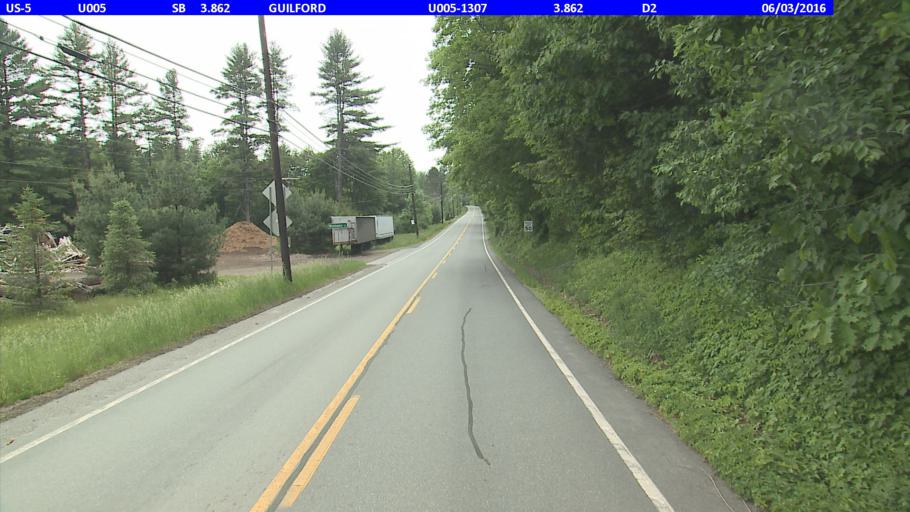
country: US
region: Vermont
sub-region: Windham County
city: Brattleboro
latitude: 42.7841
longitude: -72.5696
